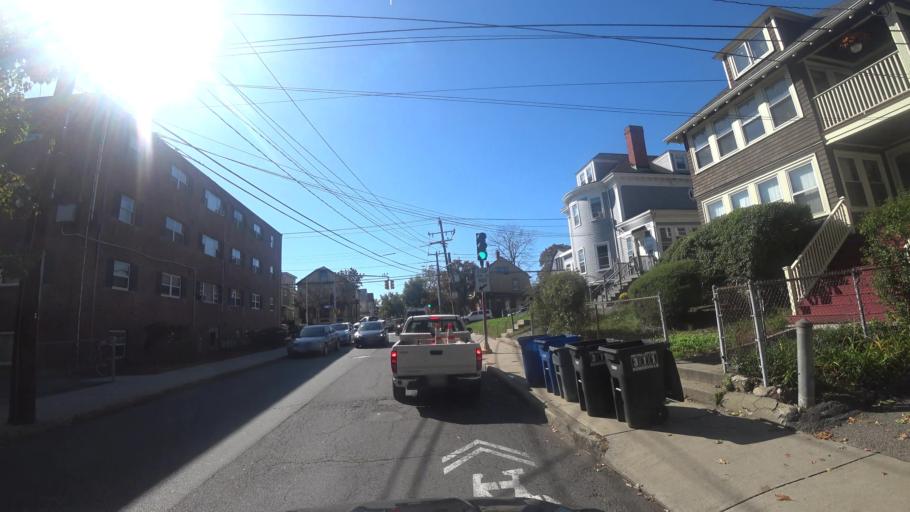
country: US
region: Massachusetts
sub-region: Middlesex County
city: Somerville
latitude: 42.3865
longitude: -71.1048
